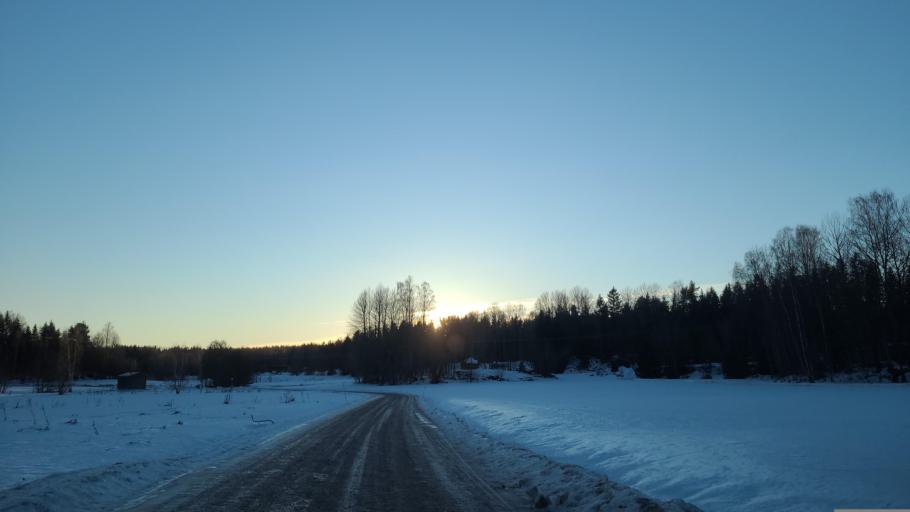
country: SE
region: Gaevleborg
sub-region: Soderhamns Kommun
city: Soderhamn
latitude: 61.2715
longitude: 16.9965
